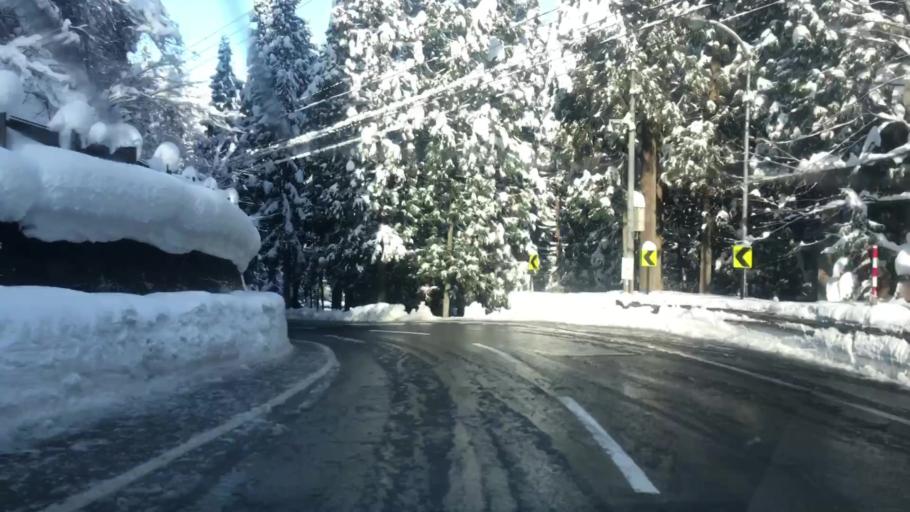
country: JP
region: Toyama
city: Kamiichi
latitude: 36.5767
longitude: 137.4050
